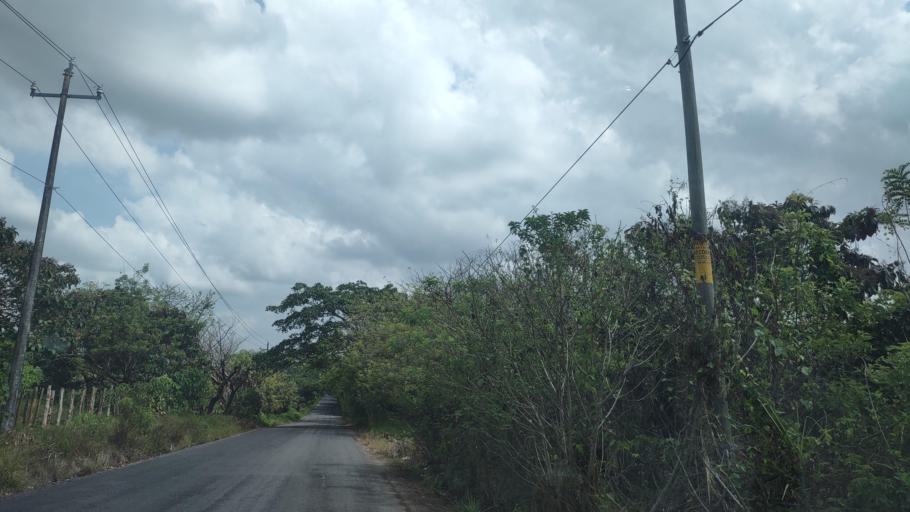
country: MX
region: Veracruz
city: Las Choapas
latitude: 17.9576
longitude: -94.1106
